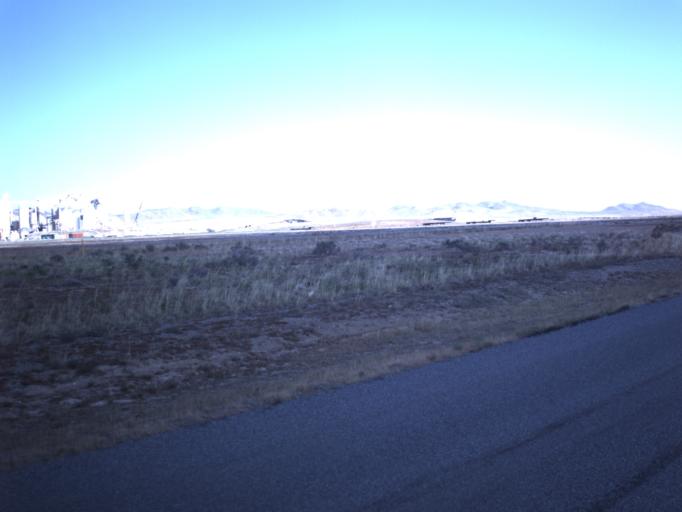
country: US
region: Utah
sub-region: Millard County
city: Delta
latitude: 38.9338
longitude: -112.8093
